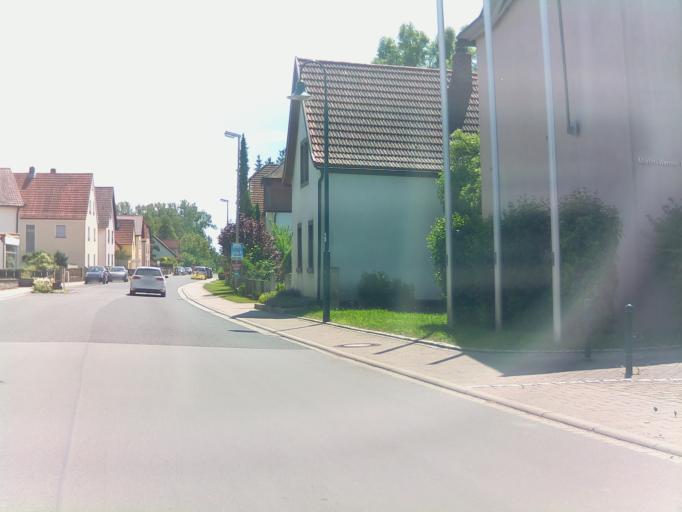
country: DE
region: Bavaria
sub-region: Regierungsbezirk Unterfranken
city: Poppenhausen
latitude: 50.0997
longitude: 10.1439
